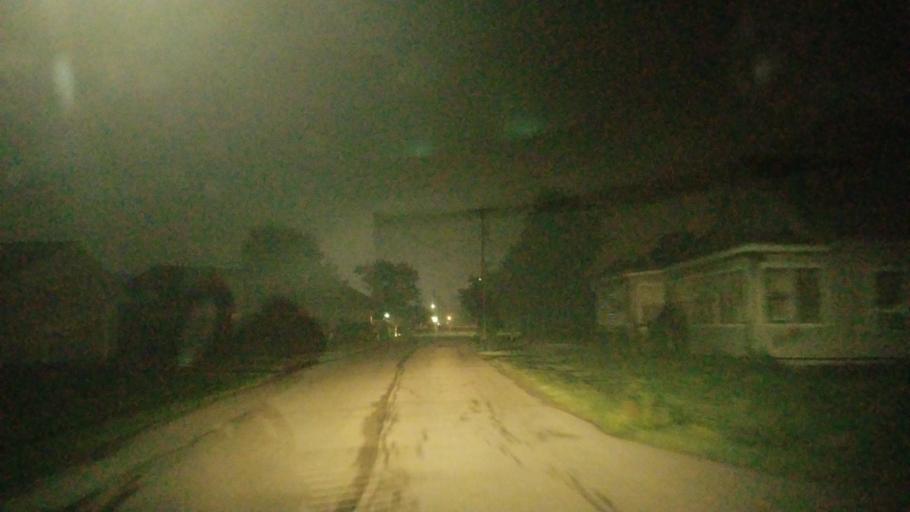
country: US
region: Missouri
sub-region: Pike County
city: Bowling Green
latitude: 39.3412
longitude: -91.1975
